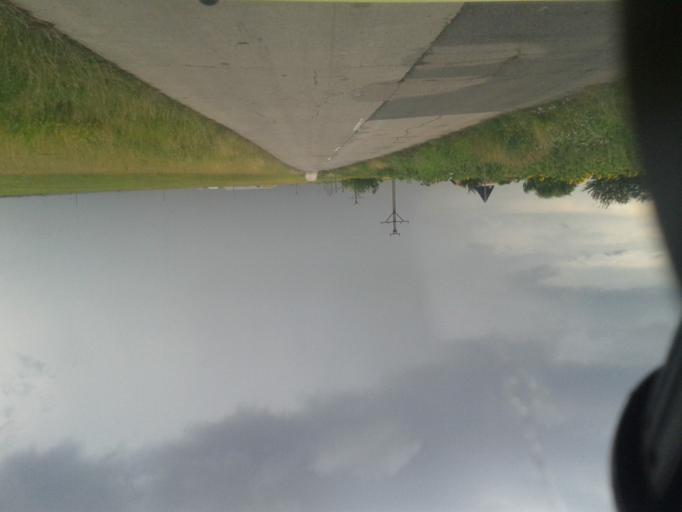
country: RO
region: Ialomita
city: Sinesti
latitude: 44.5447
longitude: 26.4204
